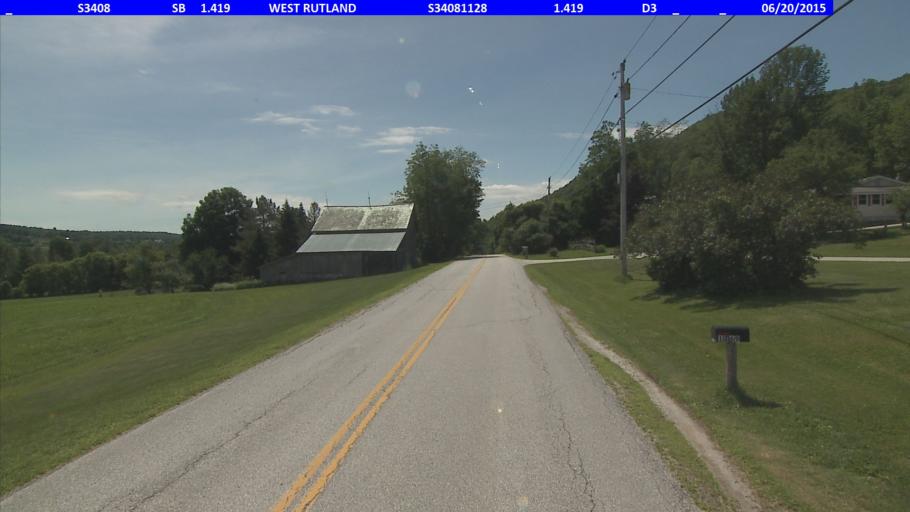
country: US
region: Vermont
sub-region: Rutland County
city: West Rutland
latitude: 43.6302
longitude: -73.0680
